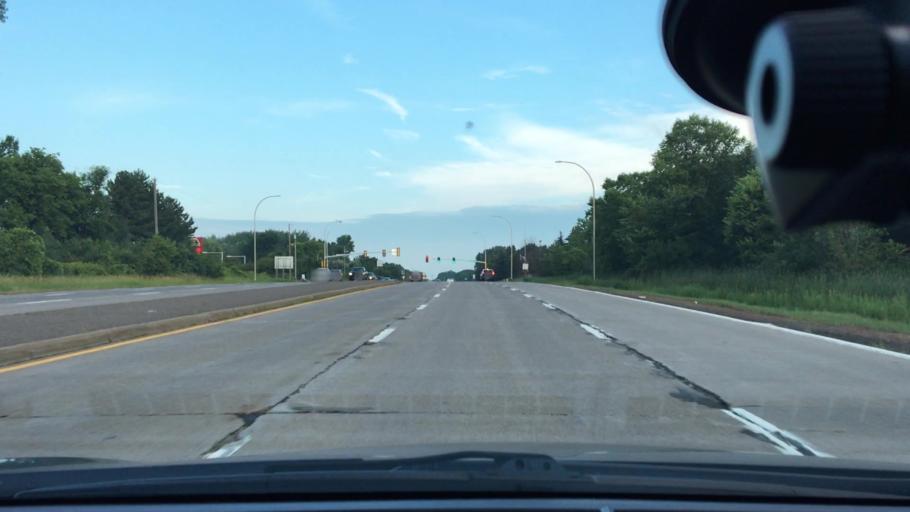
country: US
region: Minnesota
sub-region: Hennepin County
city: New Hope
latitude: 45.0585
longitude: -93.4059
